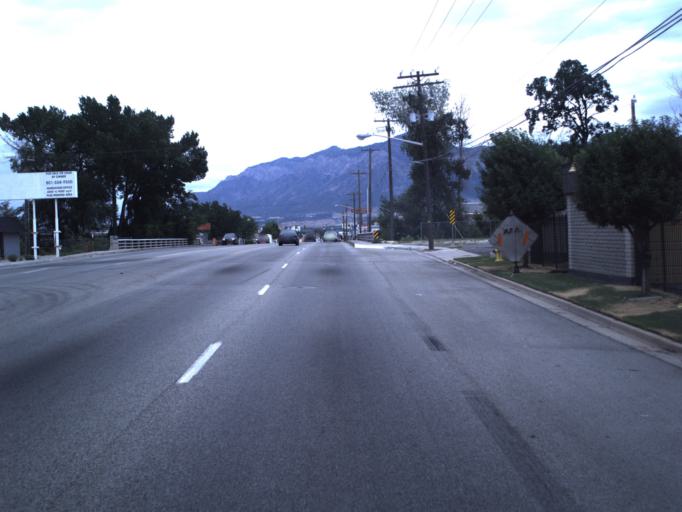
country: US
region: Utah
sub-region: Weber County
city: Ogden
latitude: 41.2334
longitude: -111.9785
